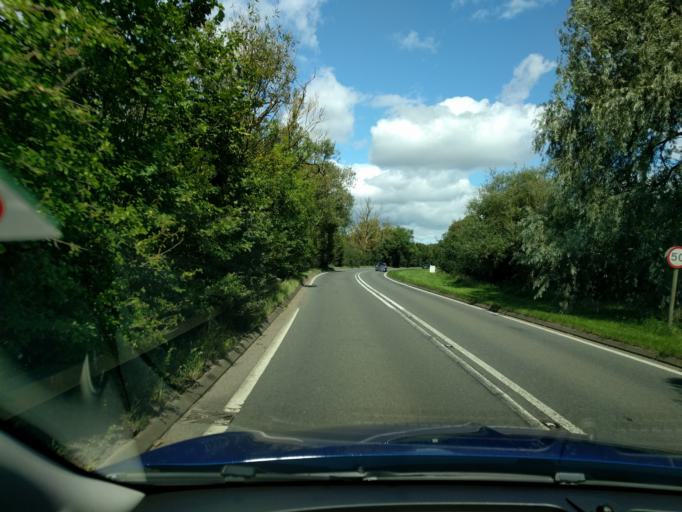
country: GB
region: England
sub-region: Gloucestershire
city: Mickleton
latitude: 52.1391
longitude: -1.7411
